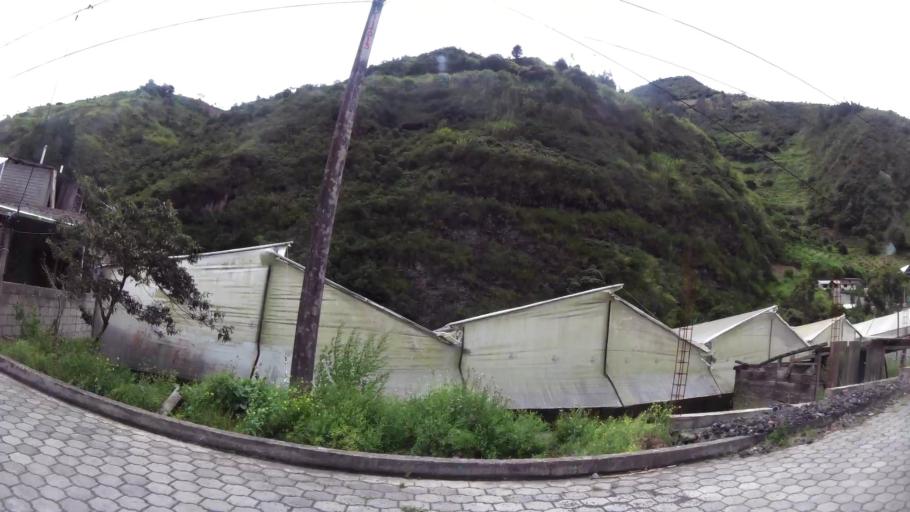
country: EC
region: Tungurahua
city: Banos
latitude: -1.3971
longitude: -78.3942
